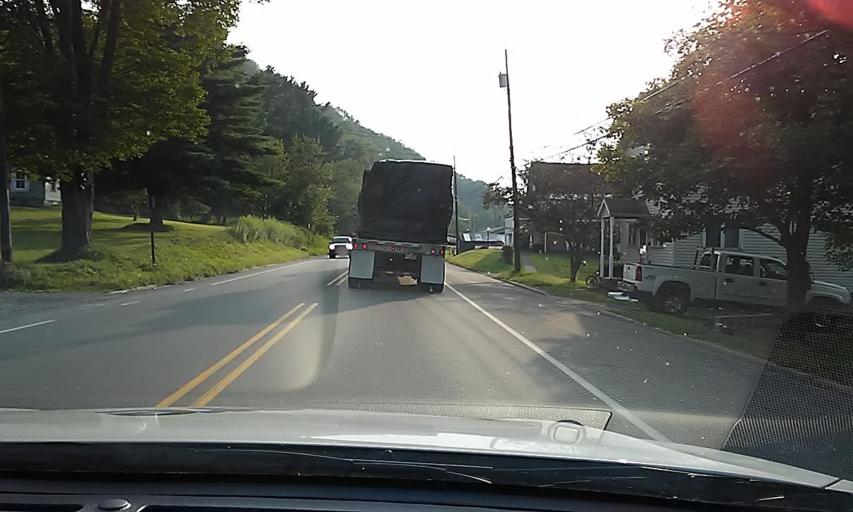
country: US
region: Pennsylvania
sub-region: McKean County
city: Smethport
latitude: 41.7053
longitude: -78.5843
